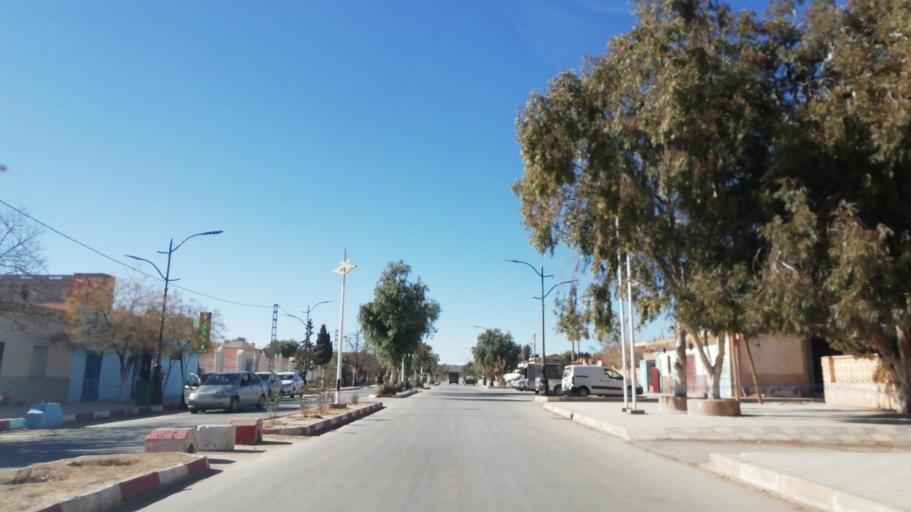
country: DZ
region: El Bayadh
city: El Bayadh
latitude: 33.7268
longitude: 1.5337
